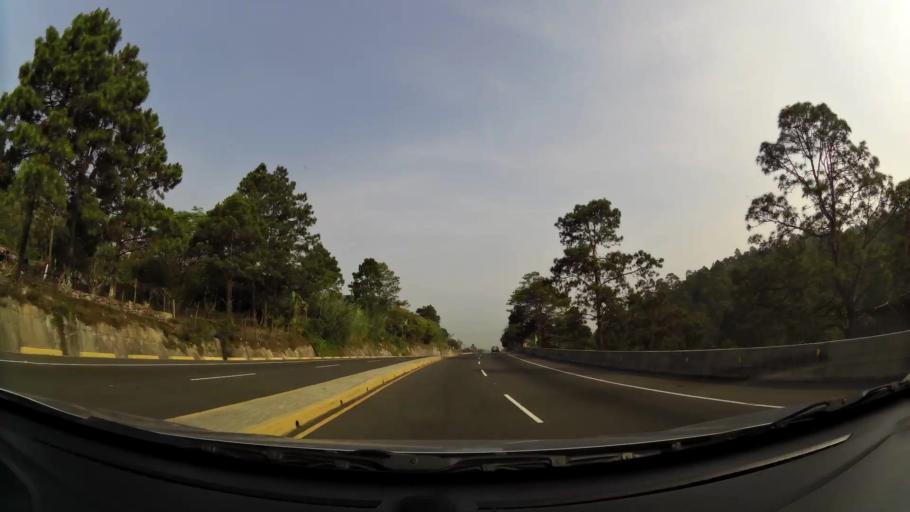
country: HN
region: Francisco Morazan
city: Zambrano
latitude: 14.2692
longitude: -87.4013
